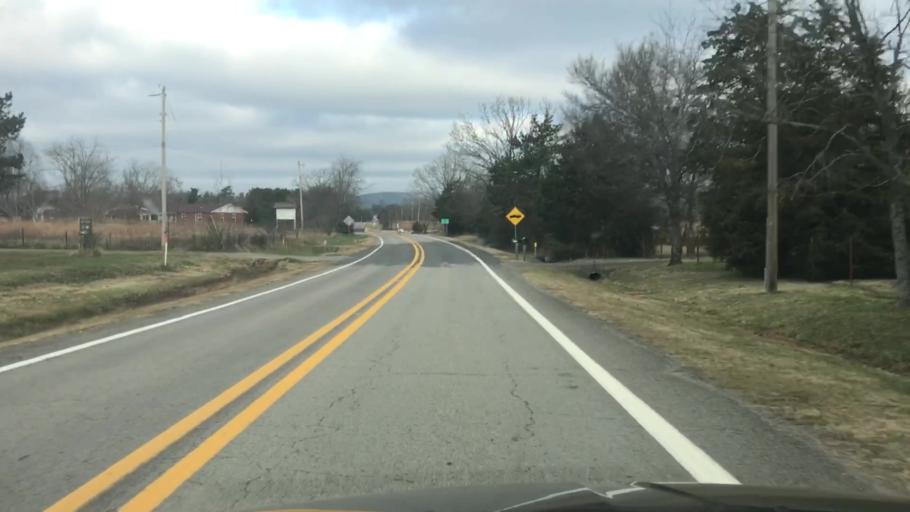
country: US
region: Arkansas
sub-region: Montgomery County
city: Mount Ida
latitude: 34.6323
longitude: -93.7357
